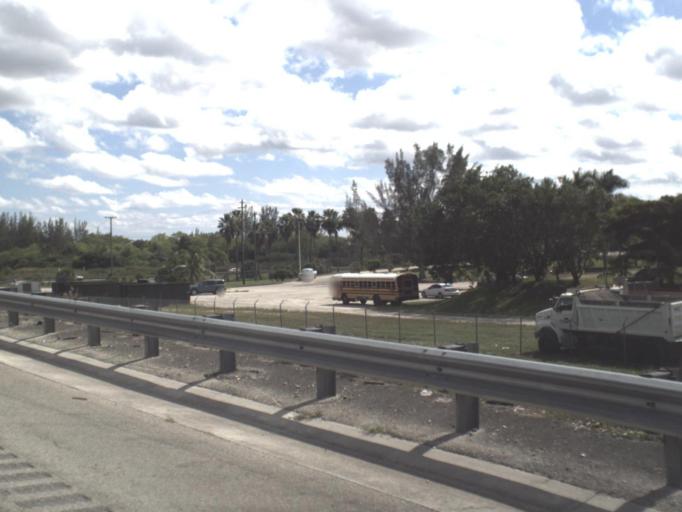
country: US
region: Florida
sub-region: Miami-Dade County
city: Lake Lucerne
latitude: 25.9712
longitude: -80.2807
